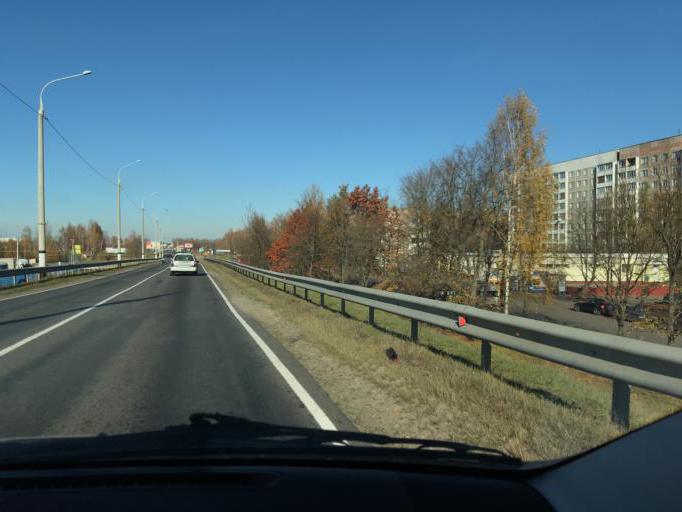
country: BY
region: Vitebsk
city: Polatsk
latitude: 55.4663
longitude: 28.7569
